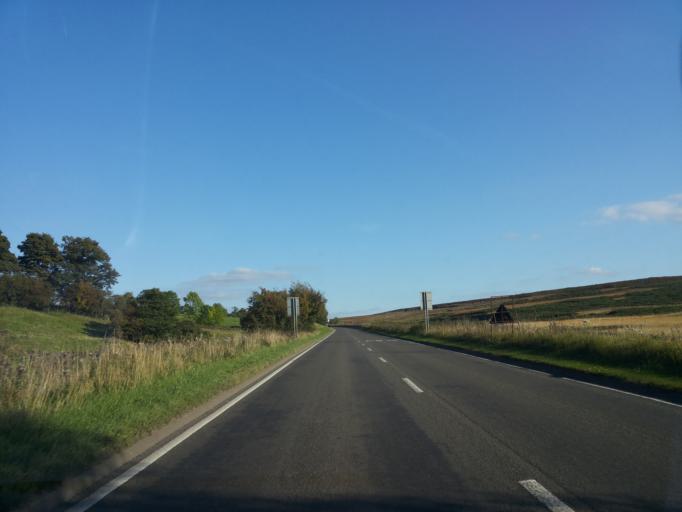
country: GB
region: England
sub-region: Derbyshire
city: Matlock
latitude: 53.2407
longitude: -1.5703
